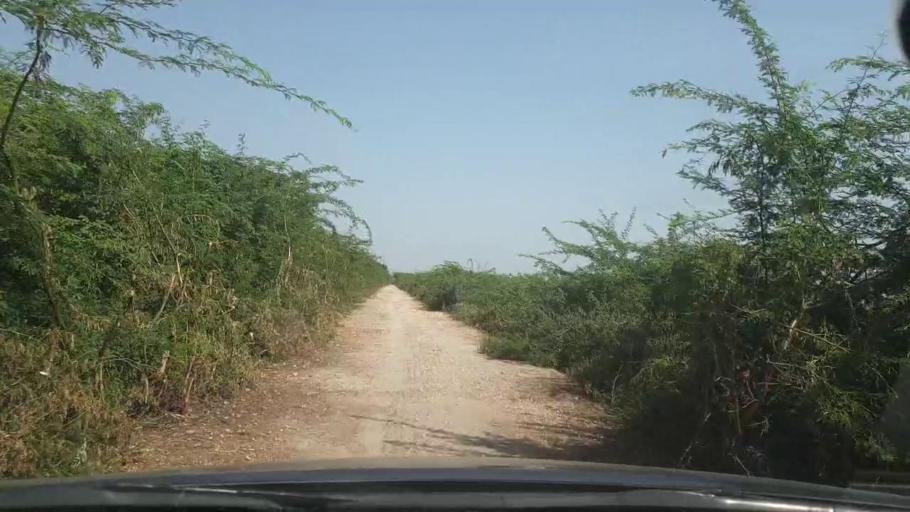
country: PK
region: Sindh
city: Naukot
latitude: 24.8088
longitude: 69.2780
